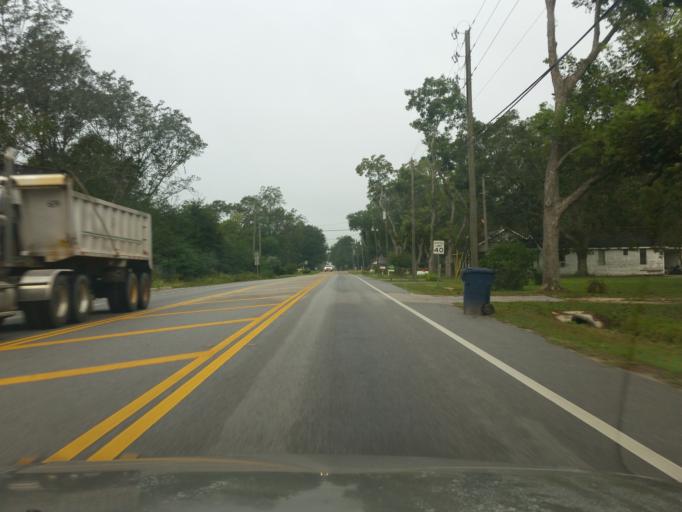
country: US
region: Florida
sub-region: Escambia County
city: Cantonment
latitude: 30.6077
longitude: -87.3576
